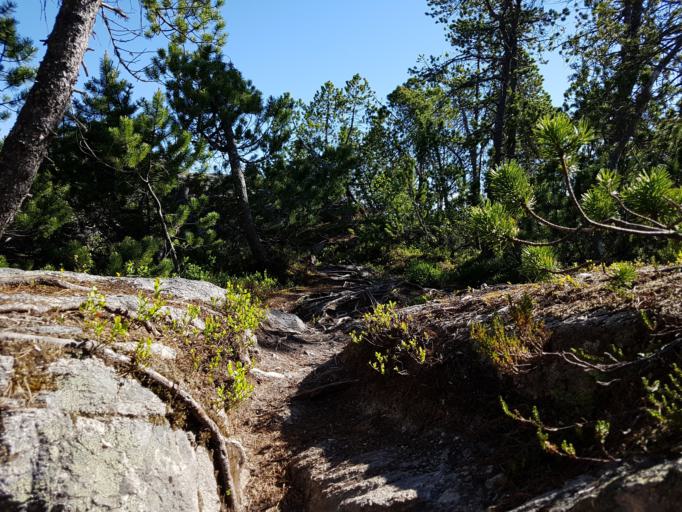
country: NO
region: Sor-Trondelag
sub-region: Trondheim
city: Trondheim
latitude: 63.4299
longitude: 10.2897
